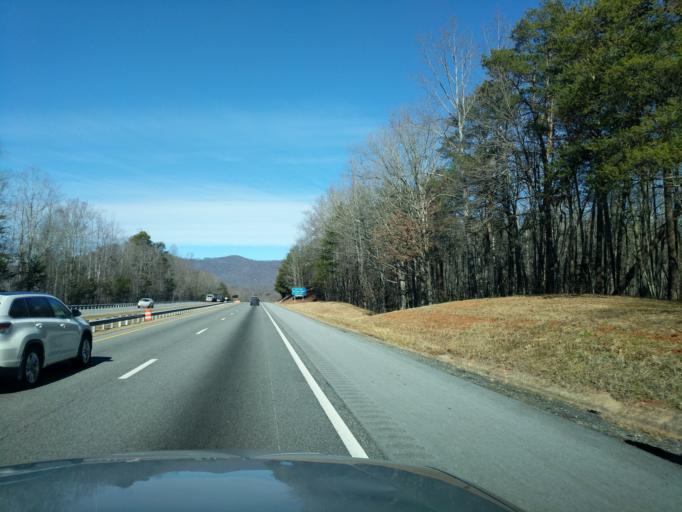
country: US
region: North Carolina
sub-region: Polk County
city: Columbus
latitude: 35.2287
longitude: -82.2000
